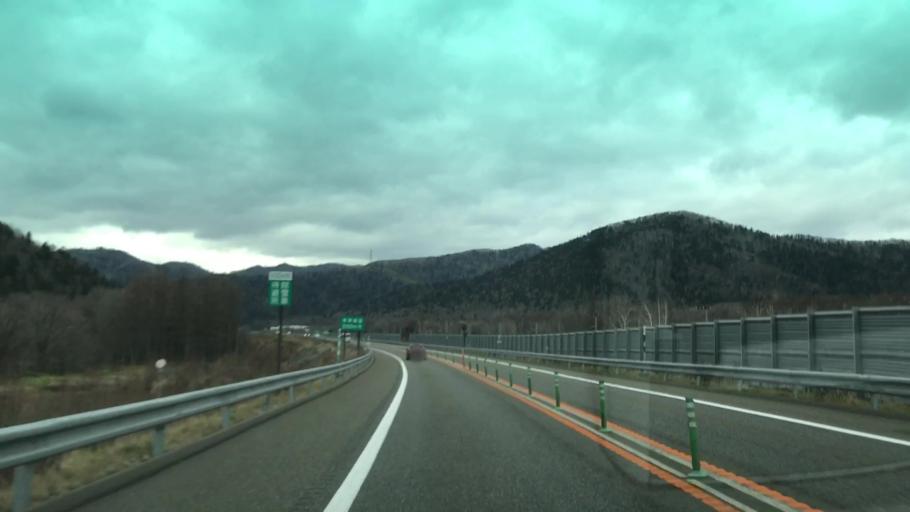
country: JP
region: Hokkaido
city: Shimo-furano
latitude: 43.0600
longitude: 142.5591
